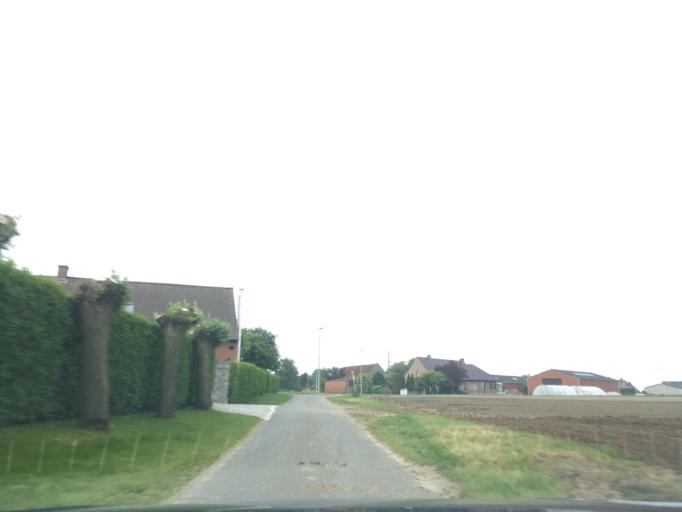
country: BE
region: Flanders
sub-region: Provincie West-Vlaanderen
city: Ingelmunster
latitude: 50.9388
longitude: 3.2626
